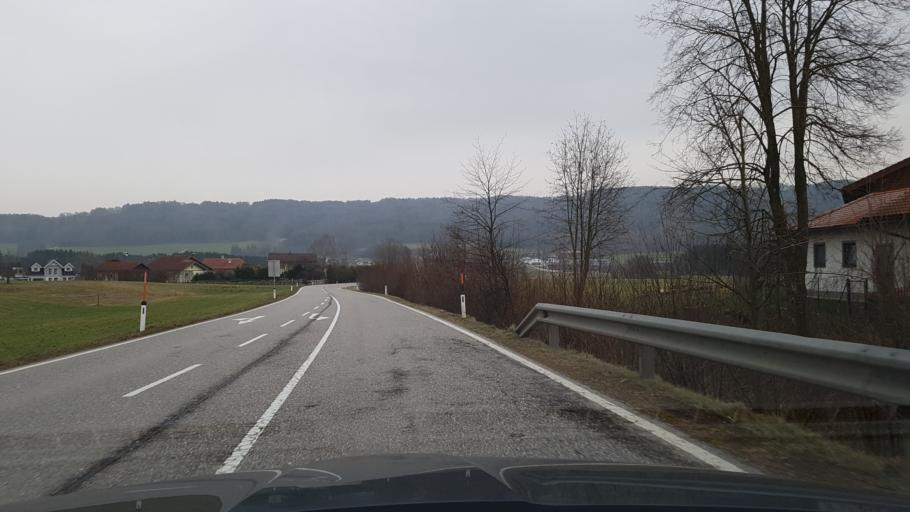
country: AT
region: Salzburg
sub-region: Politischer Bezirk Salzburg-Umgebung
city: Dorfbeuern
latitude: 48.0093
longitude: 13.0251
